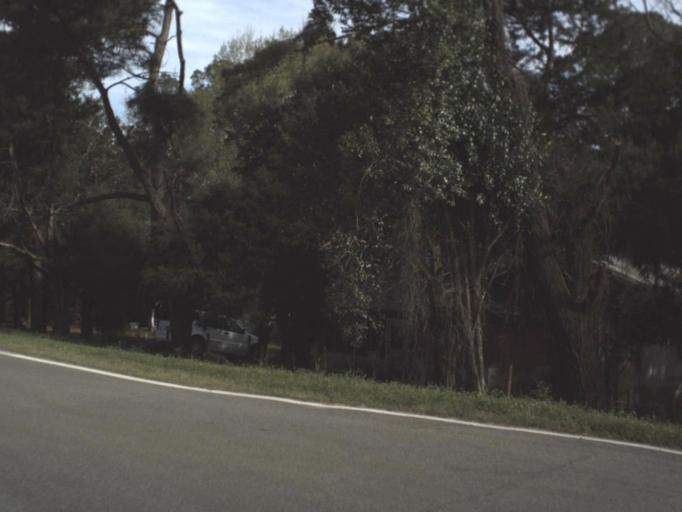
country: US
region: Florida
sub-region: Holmes County
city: Bonifay
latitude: 30.7895
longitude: -85.7012
